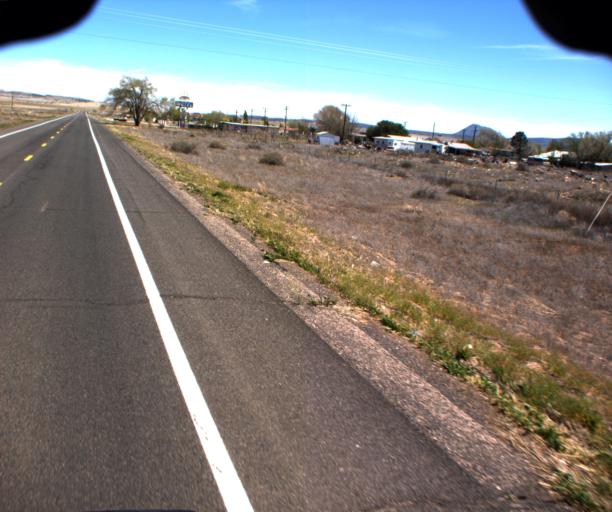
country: US
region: Arizona
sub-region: Yavapai County
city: Paulden
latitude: 35.3242
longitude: -112.8600
